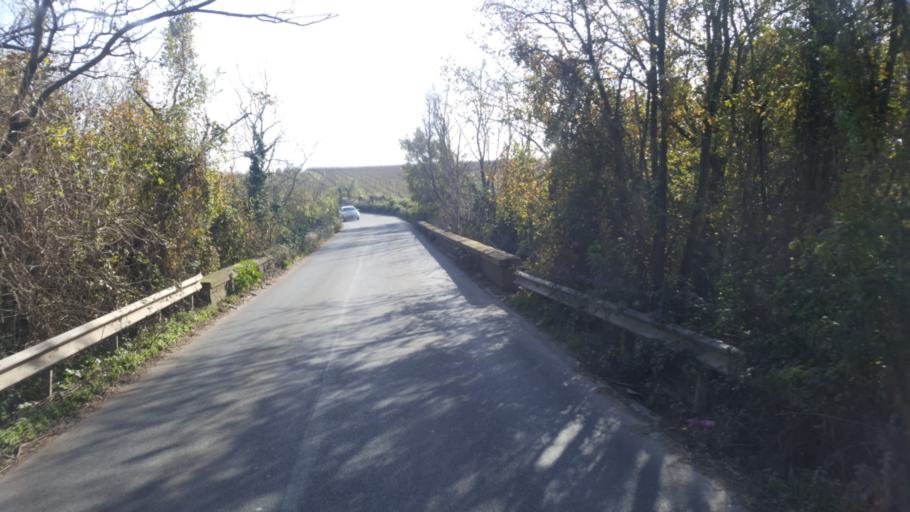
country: IT
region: Latium
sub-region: Citta metropolitana di Roma Capitale
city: Mantiglia di Ardea
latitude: 41.6889
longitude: 12.6034
